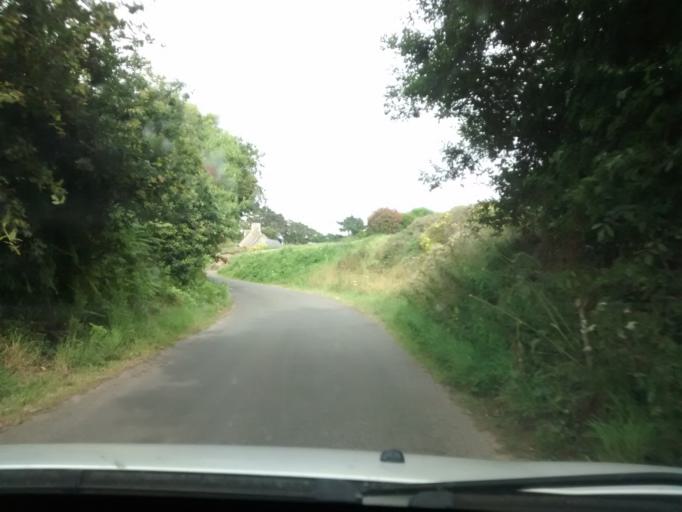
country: FR
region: Brittany
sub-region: Departement des Cotes-d'Armor
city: Penvenan
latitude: 48.8363
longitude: -3.2774
